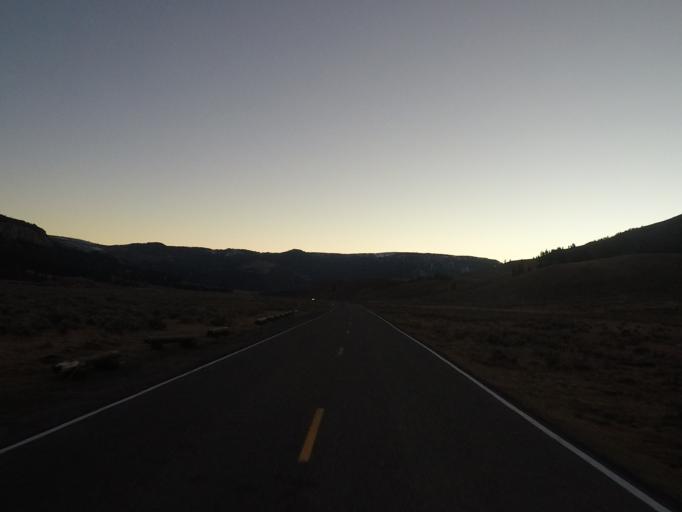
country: US
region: Montana
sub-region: Park County
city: Livingston
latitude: 44.8903
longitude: -110.1380
